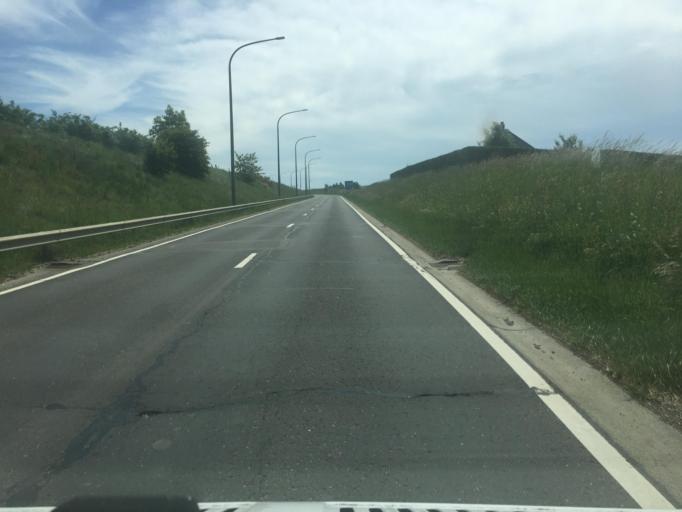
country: BE
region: Wallonia
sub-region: Province du Luxembourg
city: Bastogne
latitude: 50.0169
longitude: 5.7032
